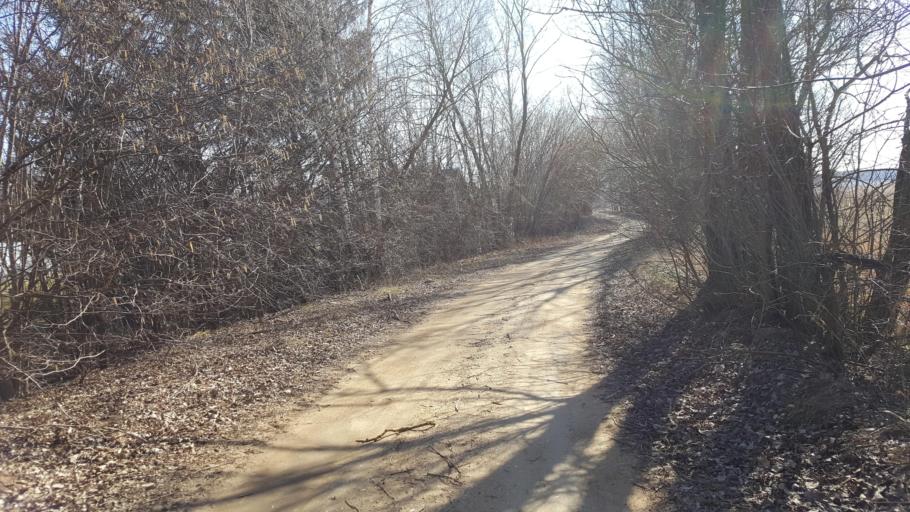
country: BY
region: Brest
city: Kamyanyets
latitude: 52.3630
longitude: 23.7620
